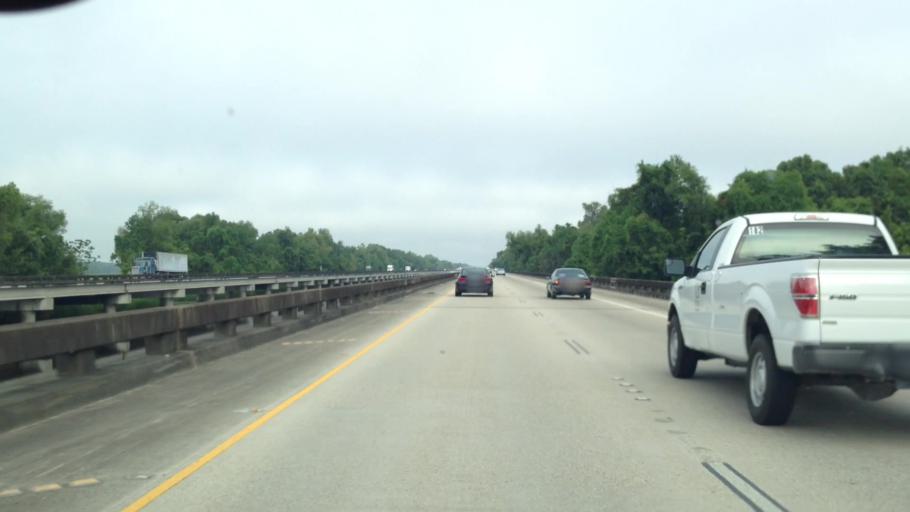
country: US
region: Louisiana
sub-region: Saint John the Baptist Parish
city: Montegut
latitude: 30.1095
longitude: -90.5251
